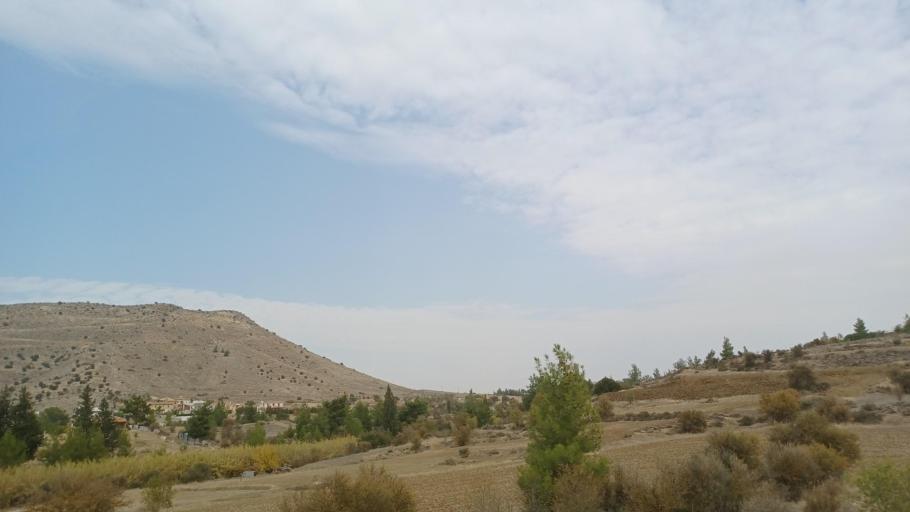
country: CY
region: Lefkosia
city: Klirou
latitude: 35.0369
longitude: 33.1339
